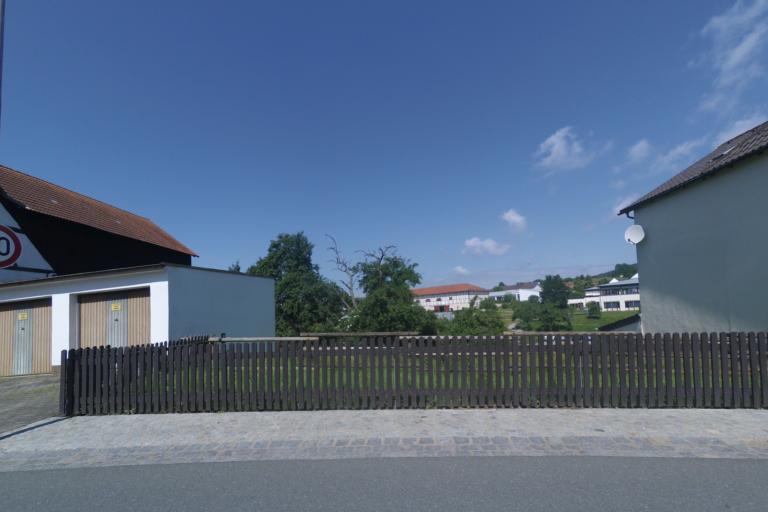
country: DE
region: Bavaria
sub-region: Upper Franconia
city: Burgkunstadt
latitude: 50.1425
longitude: 11.2536
